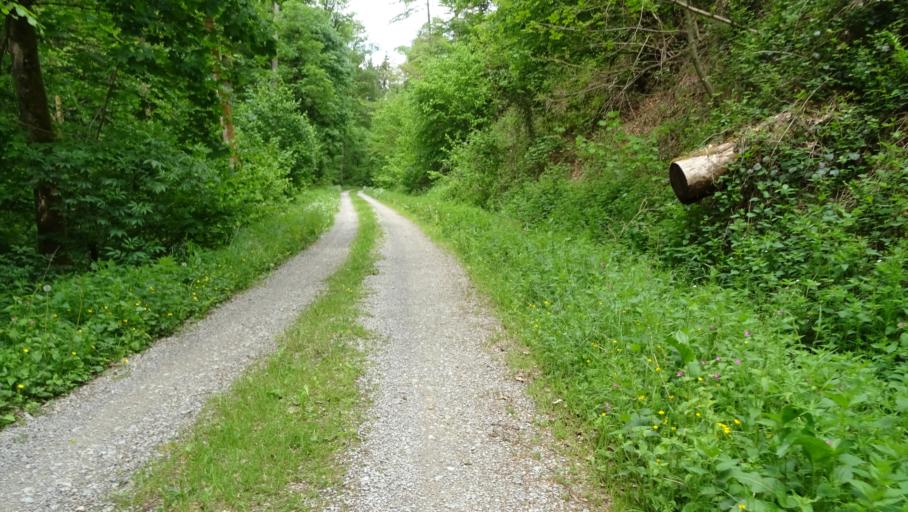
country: DE
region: Baden-Wuerttemberg
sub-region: Karlsruhe Region
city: Neckargerach
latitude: 49.4136
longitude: 9.0953
